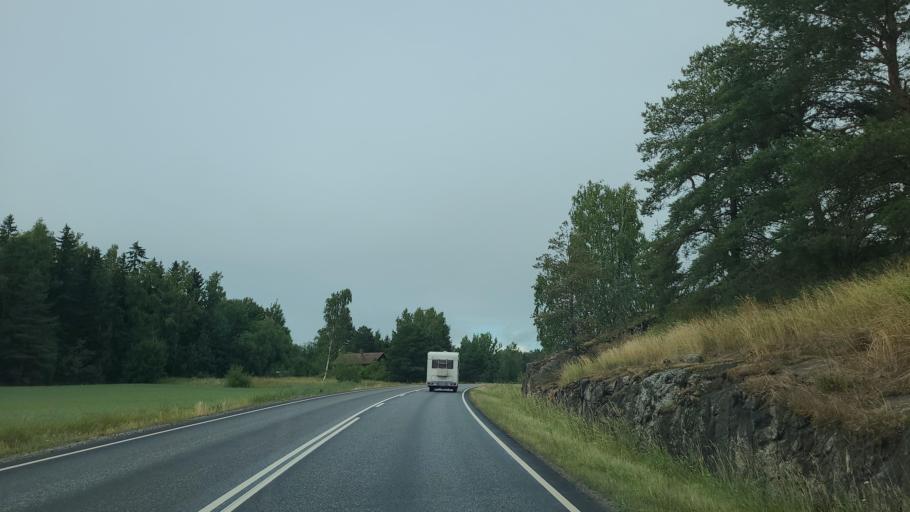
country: FI
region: Varsinais-Suomi
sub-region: Turku
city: Sauvo
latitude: 60.2913
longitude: 22.6727
